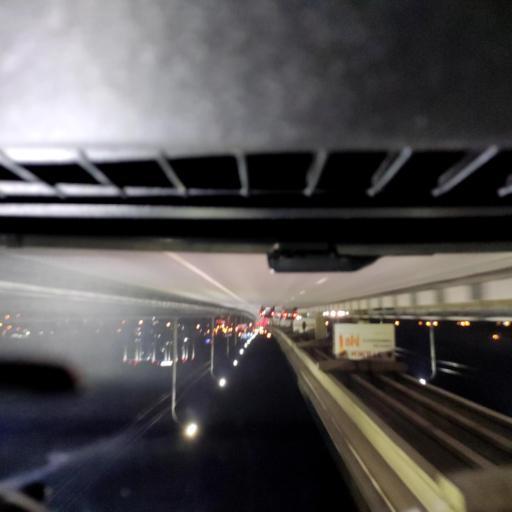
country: RU
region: Voronezj
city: Voronezh
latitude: 51.6896
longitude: 39.2439
